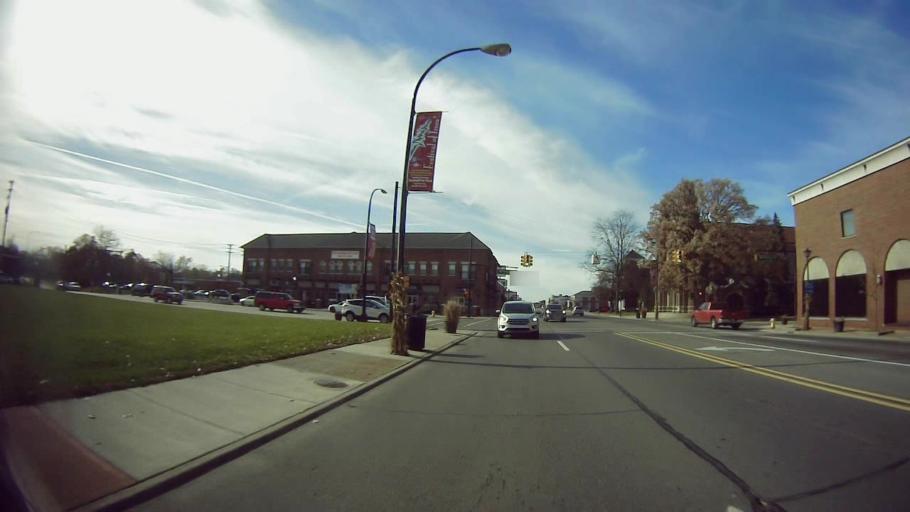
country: US
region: Michigan
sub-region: Wayne County
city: Dearborn Heights
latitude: 42.3046
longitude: -83.2506
